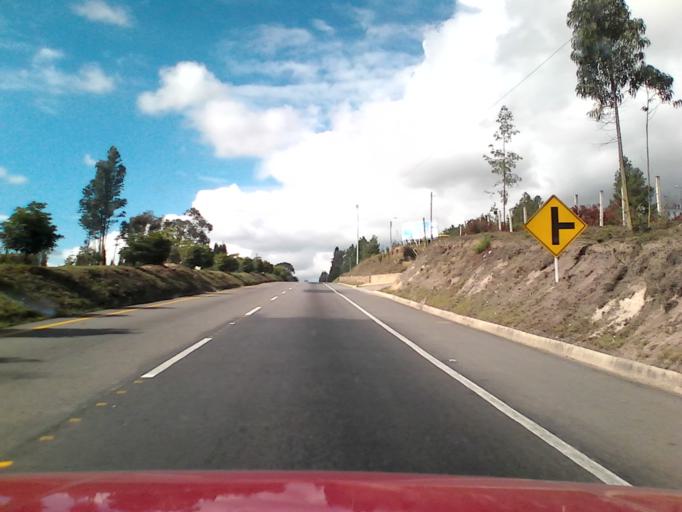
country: CO
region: Boyaca
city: Combita
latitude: 5.6370
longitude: -73.2920
